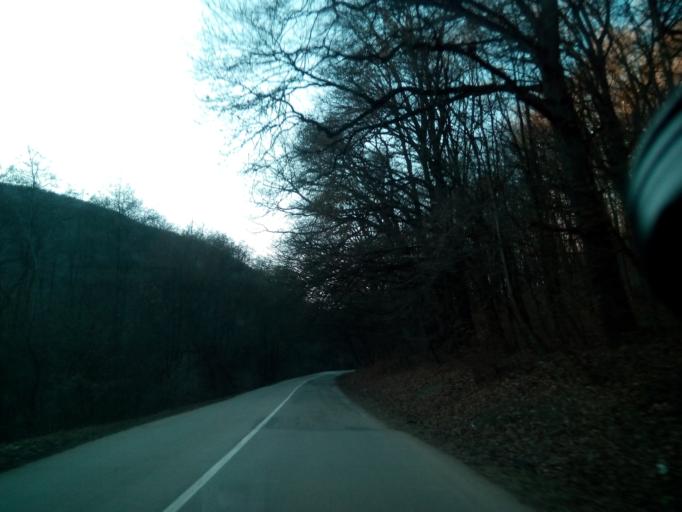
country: SK
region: Kosicky
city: Medzev
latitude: 48.6928
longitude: 20.9523
